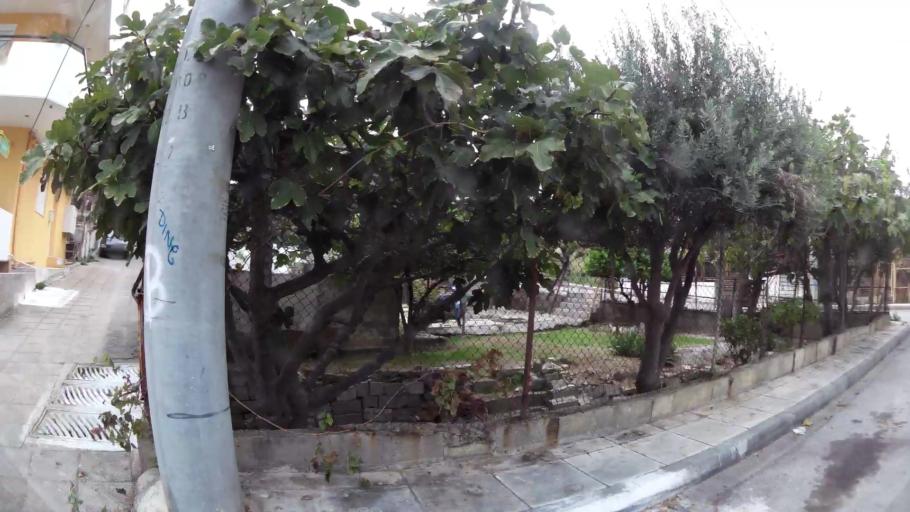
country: GR
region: Attica
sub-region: Nomarchia Athinas
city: Palaio Faliro
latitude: 37.9263
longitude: 23.7170
